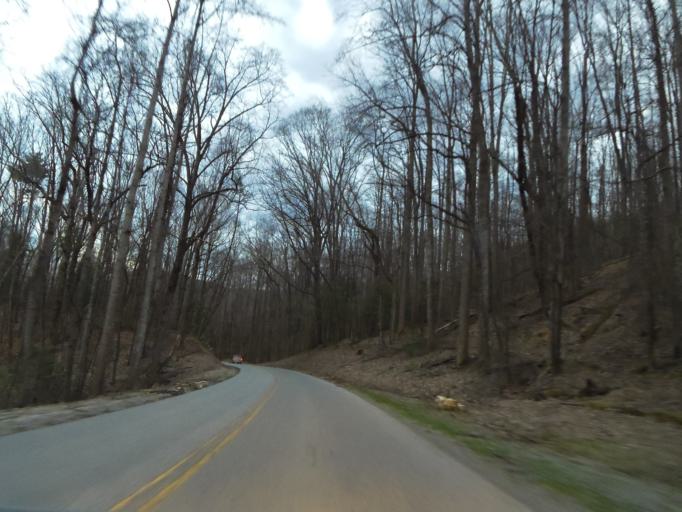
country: US
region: Tennessee
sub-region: Blount County
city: Wildwood
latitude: 35.6025
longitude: -83.7564
